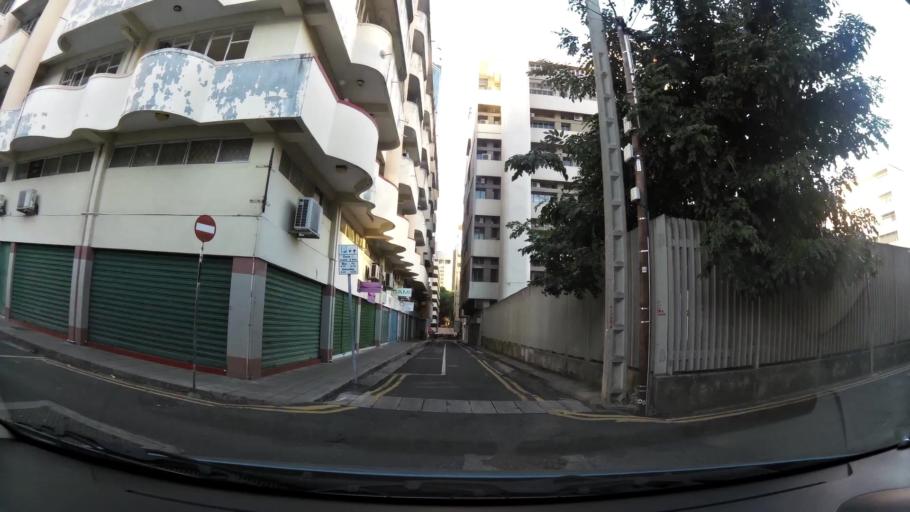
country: MU
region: Port Louis
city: Port Louis
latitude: -20.1650
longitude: 57.5004
